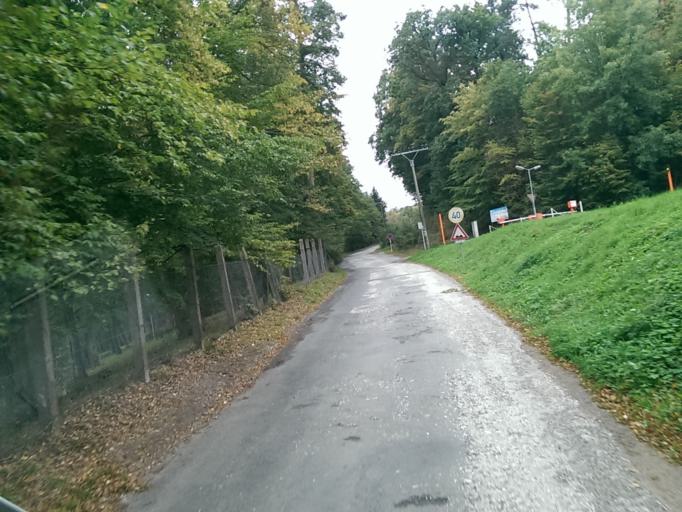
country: AT
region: Lower Austria
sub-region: Politischer Bezirk Hollabrunn
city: Hardegg
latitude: 48.9152
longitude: 15.8122
